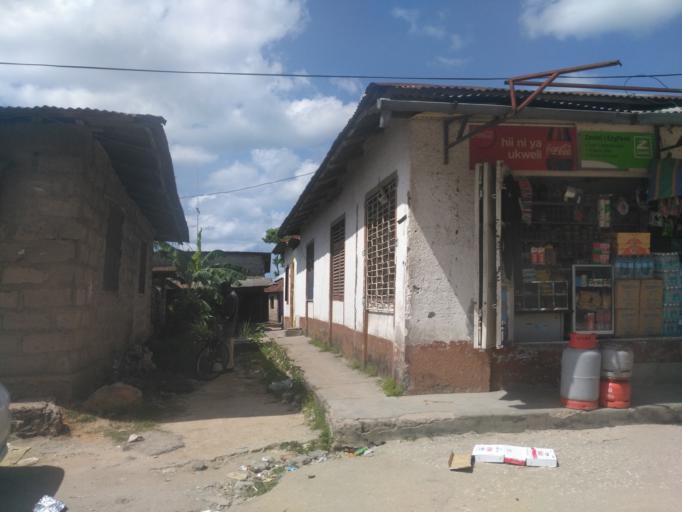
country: TZ
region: Zanzibar Urban/West
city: Zanzibar
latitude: -6.1623
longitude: 39.2079
